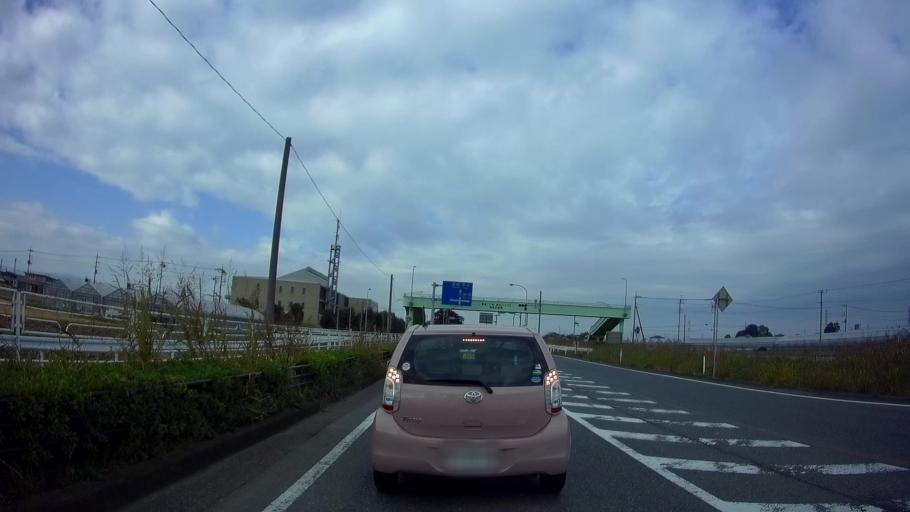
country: JP
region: Saitama
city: Fukayacho
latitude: 36.2121
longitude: 139.2869
